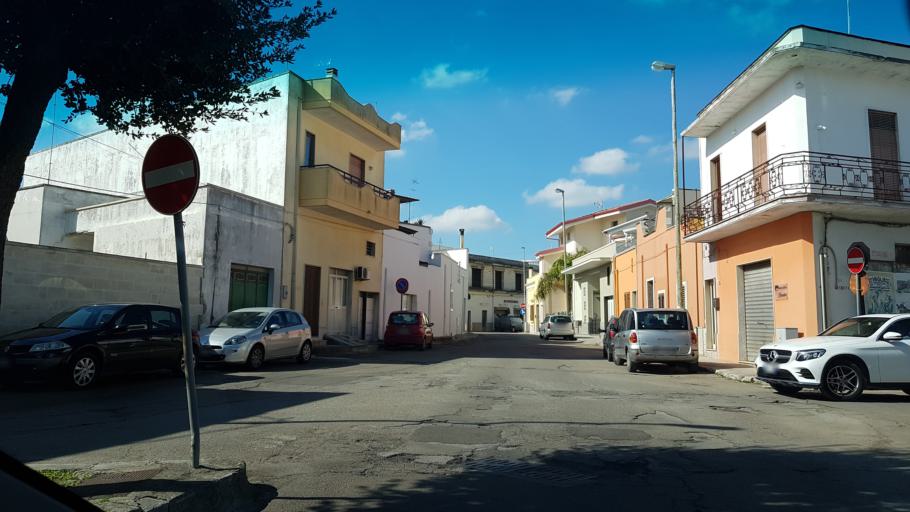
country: IT
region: Apulia
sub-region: Provincia di Lecce
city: Veglie
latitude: 40.3362
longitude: 17.9642
